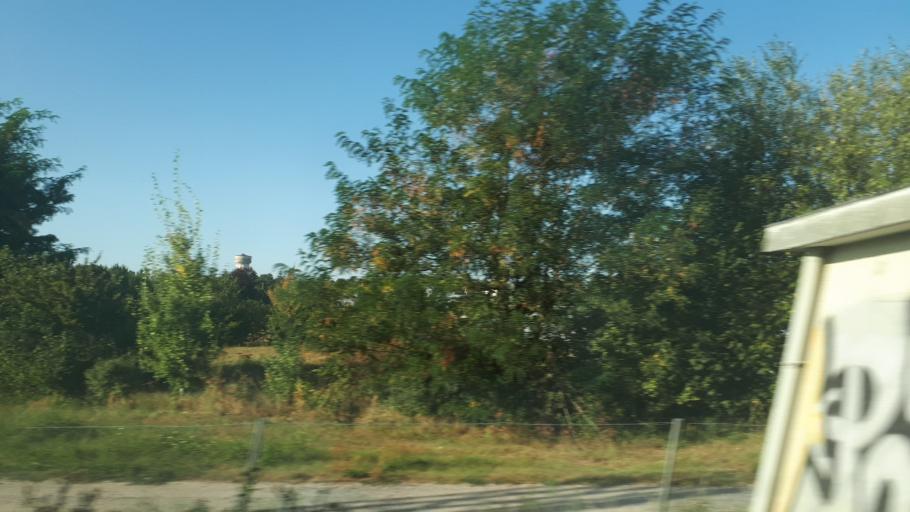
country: FR
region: Centre
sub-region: Departement d'Indre-et-Loire
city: La Ville-aux-Dames
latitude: 47.3916
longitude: 0.7708
